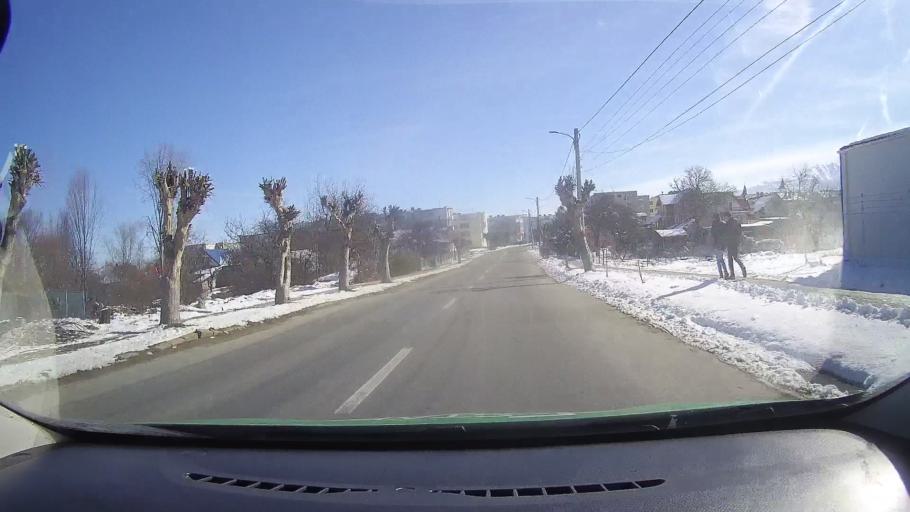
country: RO
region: Brasov
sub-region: Oras Victoria
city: Victoria
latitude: 45.7344
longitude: 24.6977
